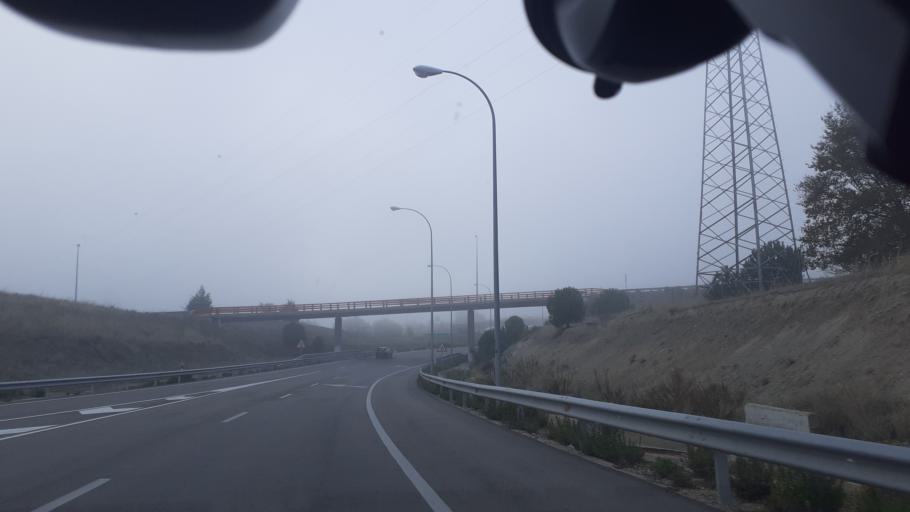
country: ES
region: Madrid
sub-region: Provincia de Madrid
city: Villa de Vallecas
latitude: 40.3753
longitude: -3.5976
